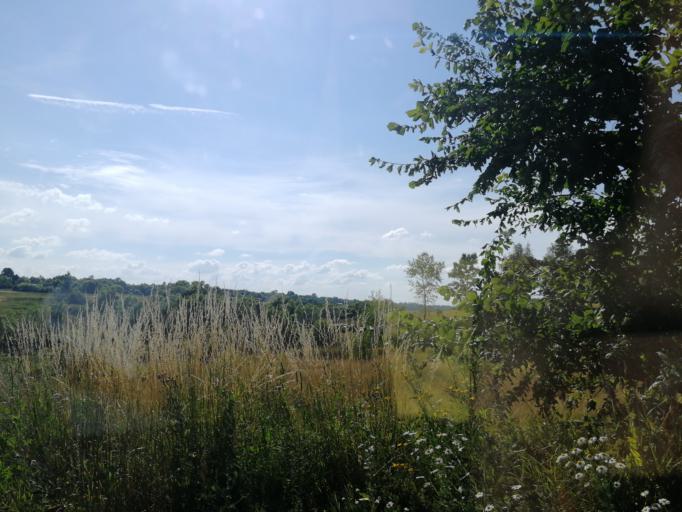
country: RU
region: Tula
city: Tovarkovskiy
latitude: 53.6077
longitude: 38.2722
